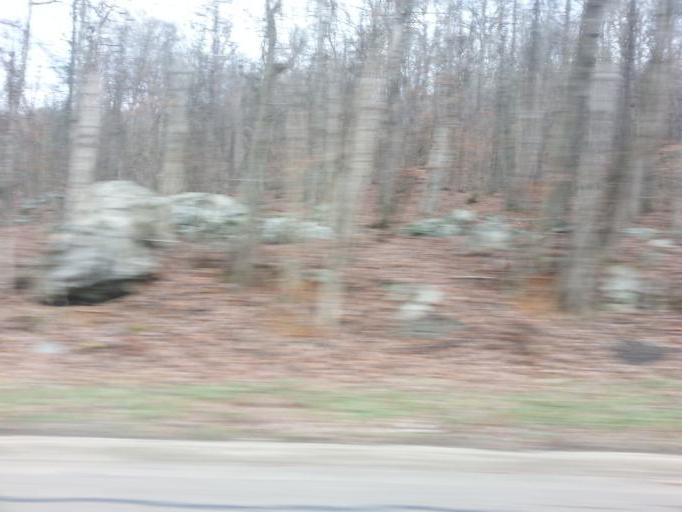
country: US
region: Tennessee
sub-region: Hamilton County
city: Sale Creek
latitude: 35.4060
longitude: -85.1019
